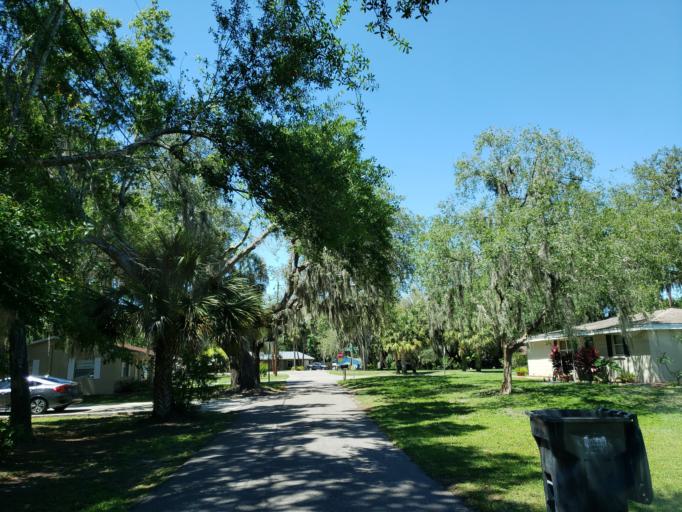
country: US
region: Florida
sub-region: Hillsborough County
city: Riverview
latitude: 27.8623
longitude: -82.3186
